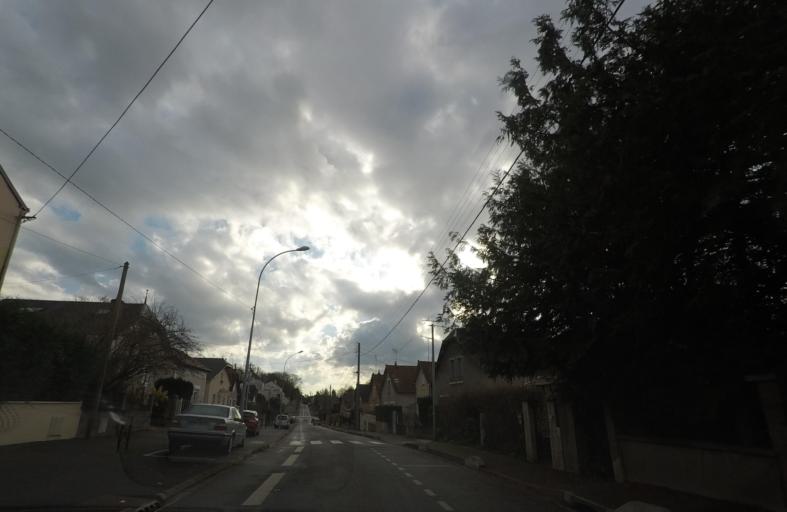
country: FR
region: Centre
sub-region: Departement du Cher
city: Bourges
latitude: 47.0647
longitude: 2.3996
